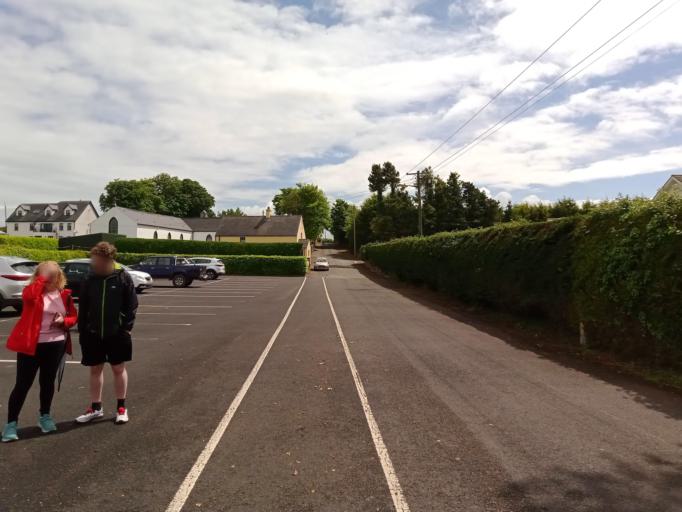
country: IE
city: Ballylinan
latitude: 52.9661
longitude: -7.0787
